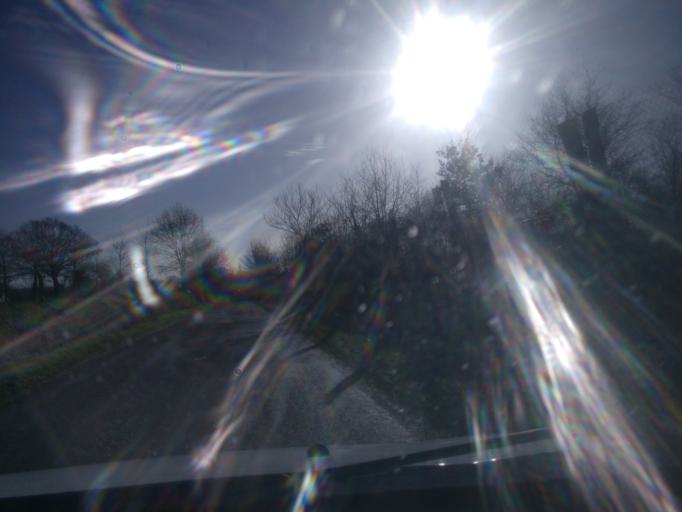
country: FR
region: Brittany
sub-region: Departement d'Ille-et-Vilaine
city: Pleine-Fougeres
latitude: 48.5322
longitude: -1.5374
